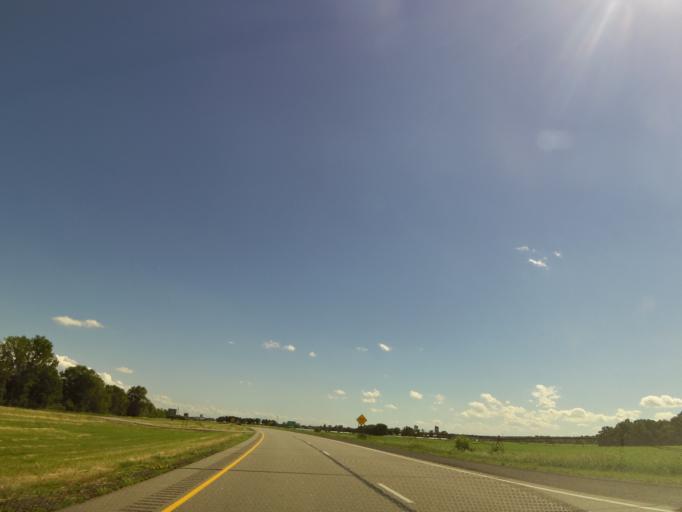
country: US
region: Minnesota
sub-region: Stearns County
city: Saint Augusta
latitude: 45.4896
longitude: -94.2464
